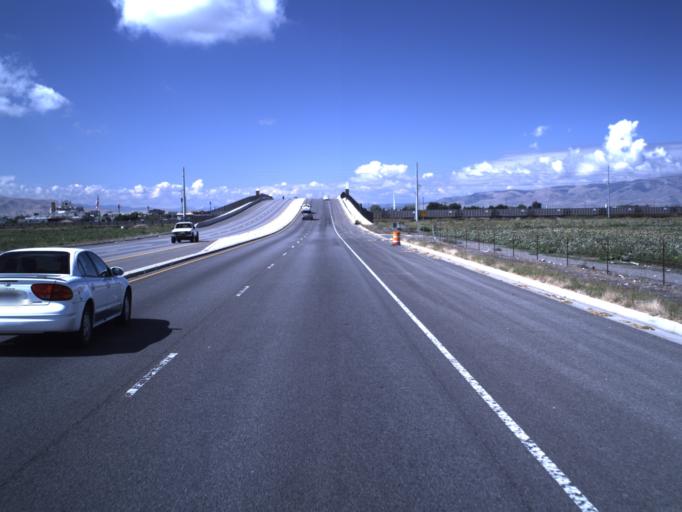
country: US
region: Utah
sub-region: Utah County
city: Springville
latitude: 40.1614
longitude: -111.6331
